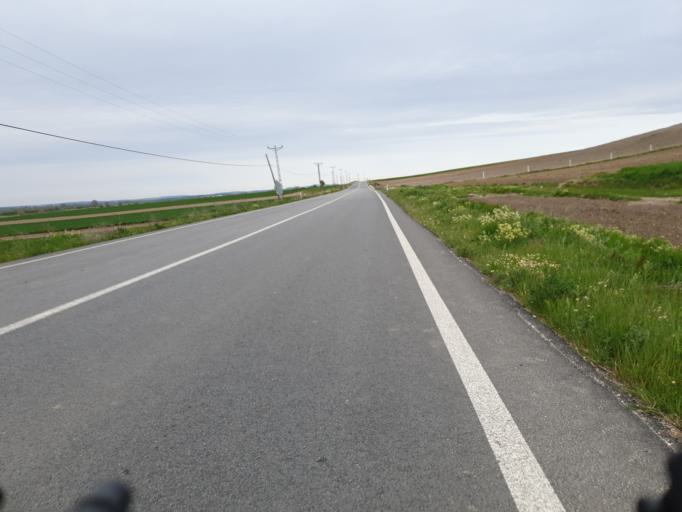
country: TR
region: Tekirdag
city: Velimese
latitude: 41.3515
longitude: 27.8413
